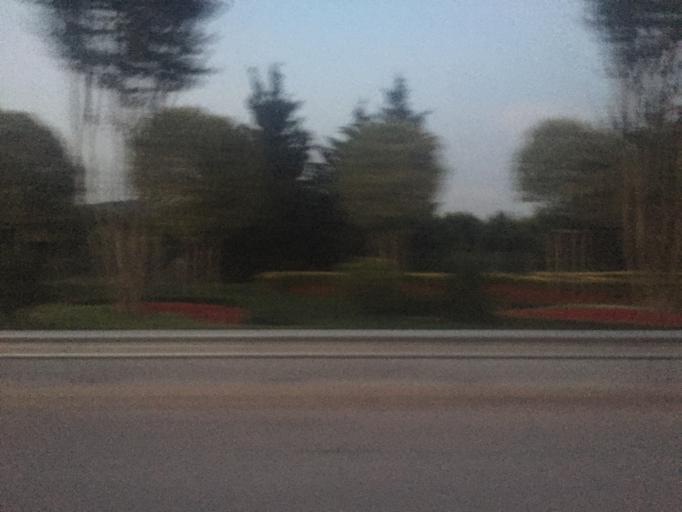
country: TR
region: Istanbul
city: Pendik
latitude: 40.9130
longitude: 29.3132
